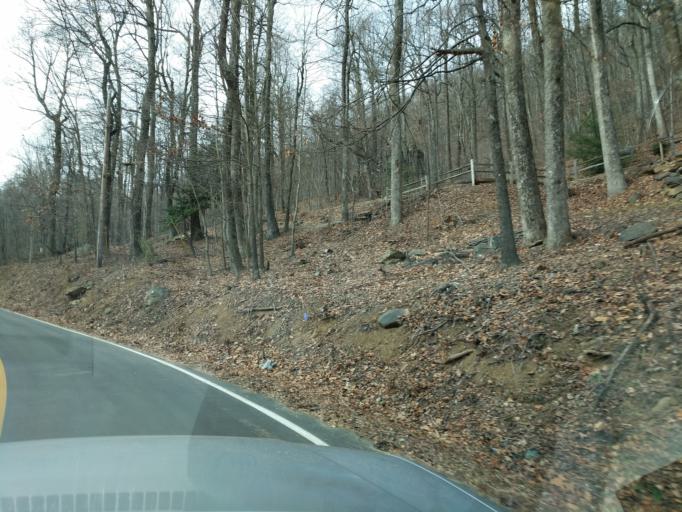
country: US
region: North Carolina
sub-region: Polk County
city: Columbus
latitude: 35.2695
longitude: -82.2310
